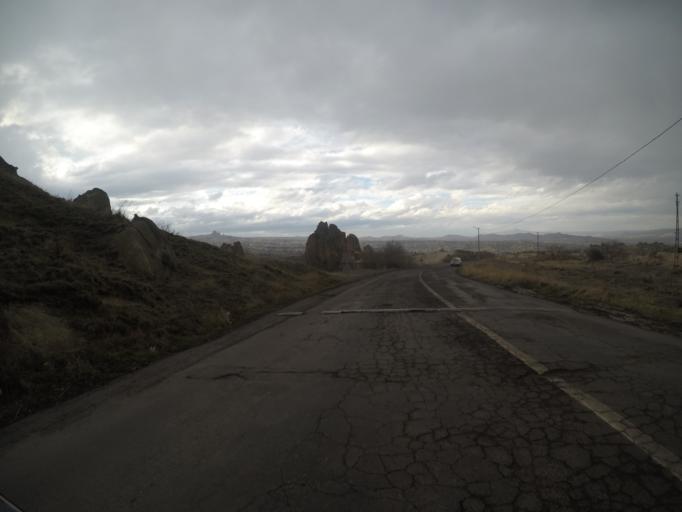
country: TR
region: Nevsehir
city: Goereme
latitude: 38.6370
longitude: 34.8525
